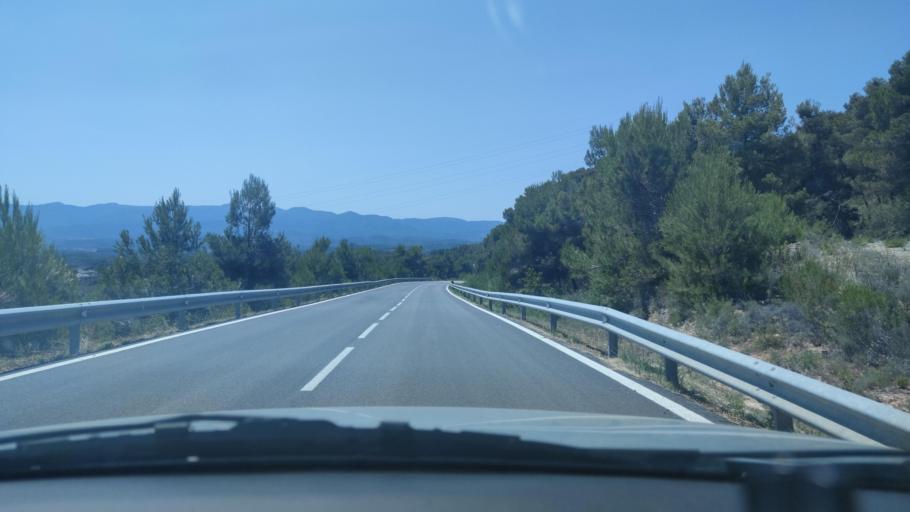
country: ES
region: Catalonia
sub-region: Provincia de Lleida
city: Fulleda
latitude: 41.4331
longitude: 1.0326
